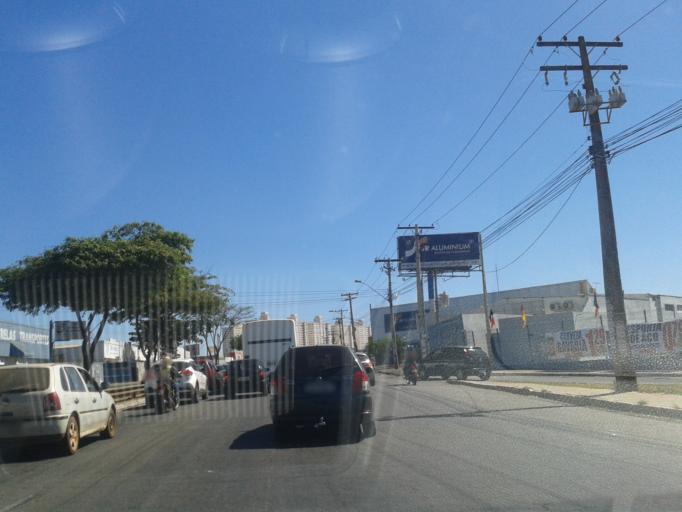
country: BR
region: Goias
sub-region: Goiania
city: Goiania
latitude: -16.6517
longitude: -49.3180
